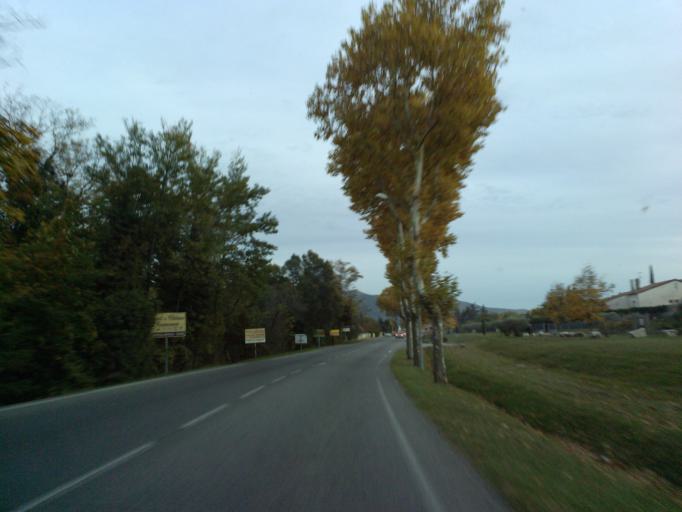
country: FR
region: Provence-Alpes-Cote d'Azur
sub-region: Departement des Alpes-de-Haute-Provence
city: Volonne
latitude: 44.1047
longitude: 6.0068
